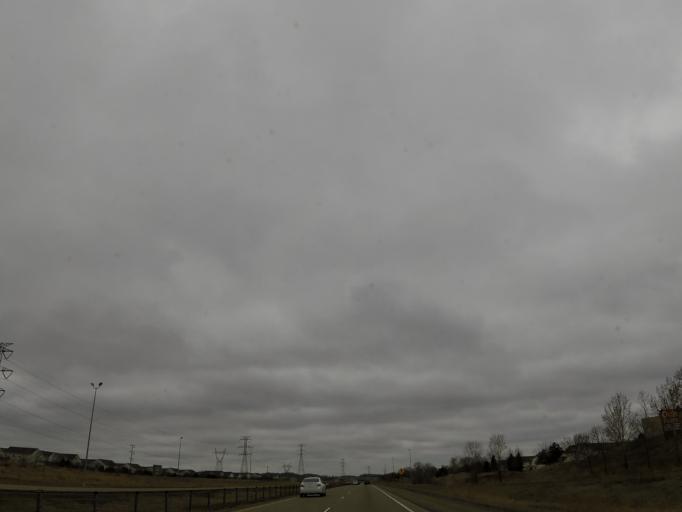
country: US
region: Minnesota
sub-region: Scott County
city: Shakopee
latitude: 44.7778
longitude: -93.5084
